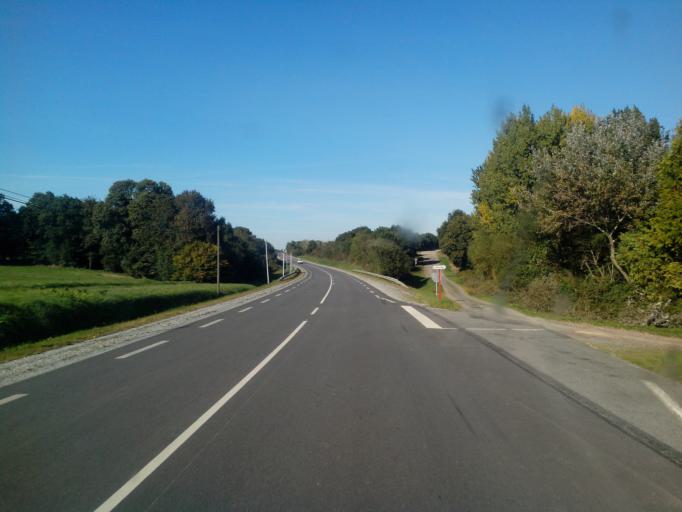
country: FR
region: Brittany
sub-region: Departement du Morbihan
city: Mauron
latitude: 48.0598
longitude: -2.2923
